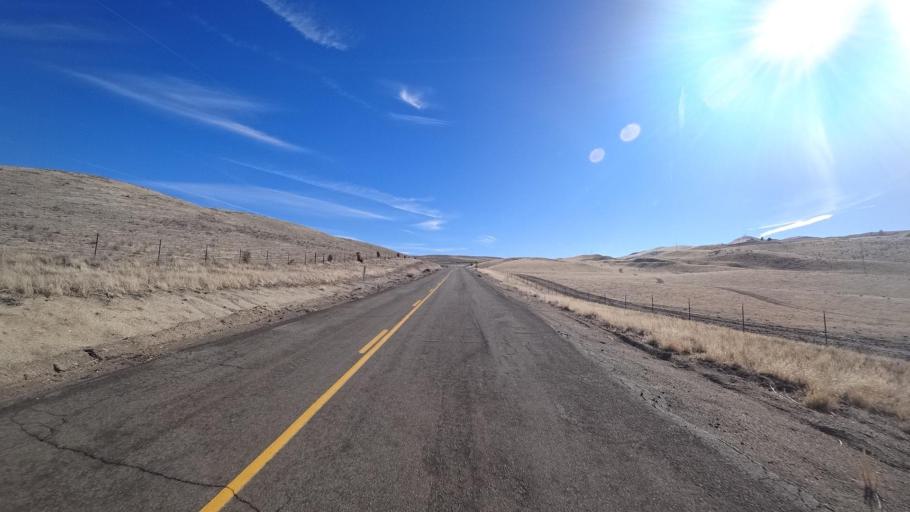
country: US
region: California
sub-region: Kern County
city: Maricopa
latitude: 34.9476
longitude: -119.4173
